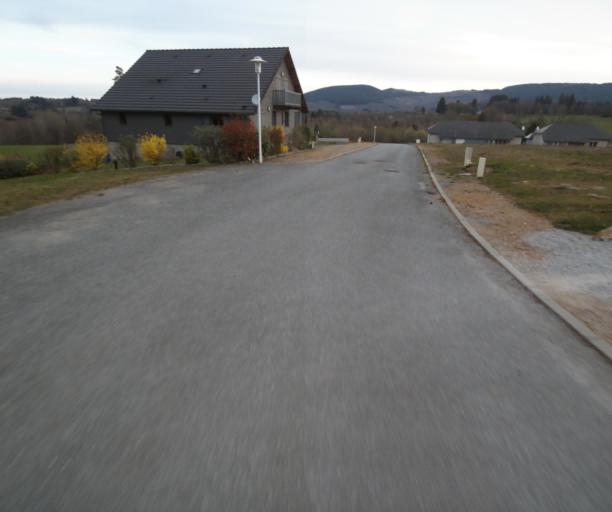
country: FR
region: Limousin
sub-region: Departement de la Correze
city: Correze
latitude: 45.4296
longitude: 1.8358
